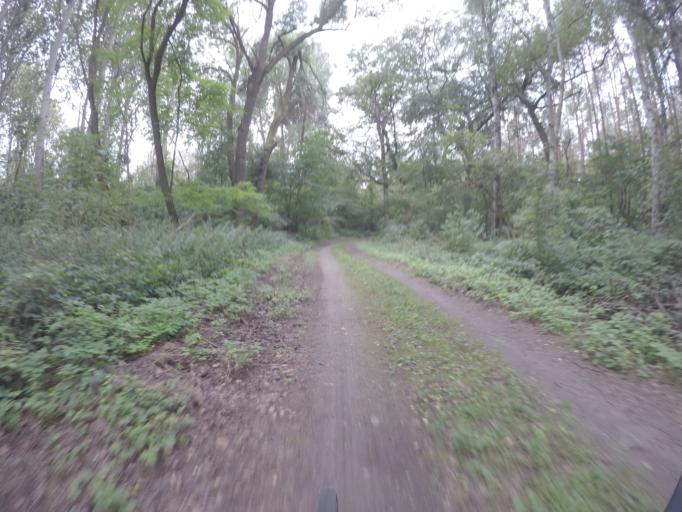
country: DE
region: Brandenburg
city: Brieselang
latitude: 52.6147
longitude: 13.0206
